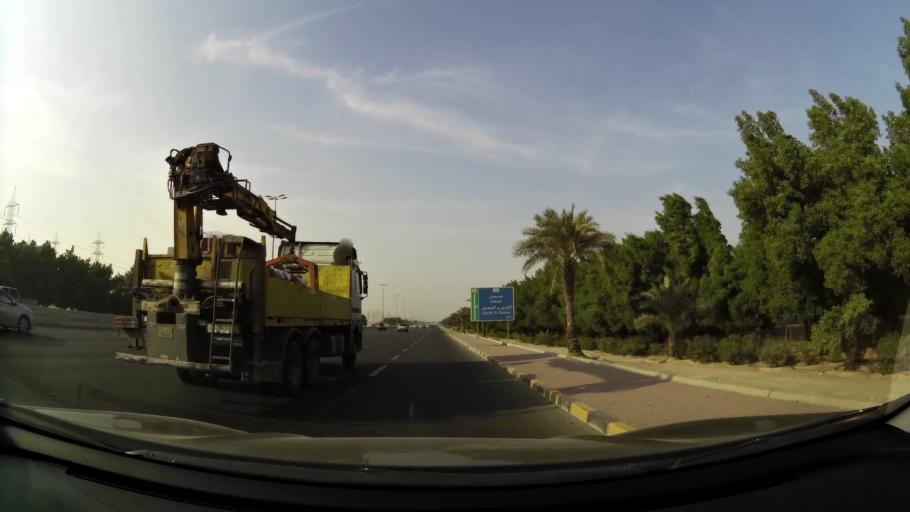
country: KW
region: Mubarak al Kabir
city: Mubarak al Kabir
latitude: 29.1947
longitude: 48.0632
